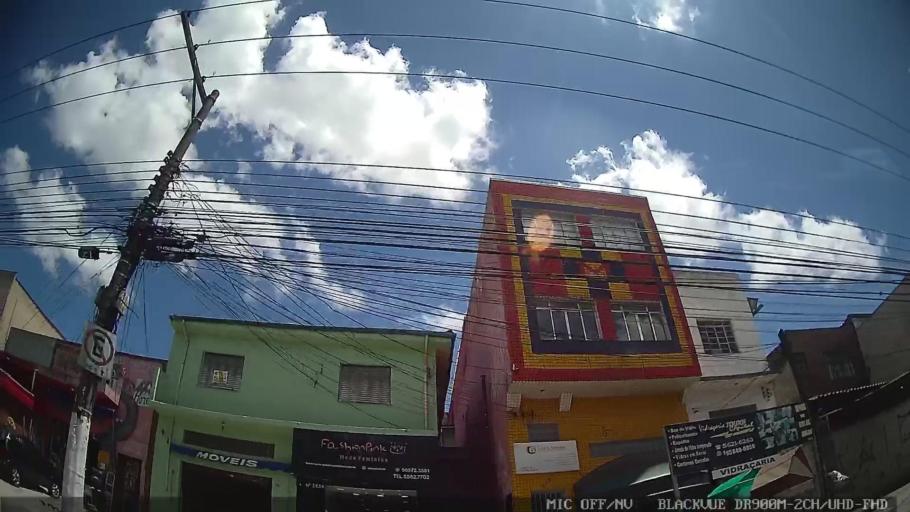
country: BR
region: Sao Paulo
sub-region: Diadema
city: Diadema
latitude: -23.6693
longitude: -46.6500
